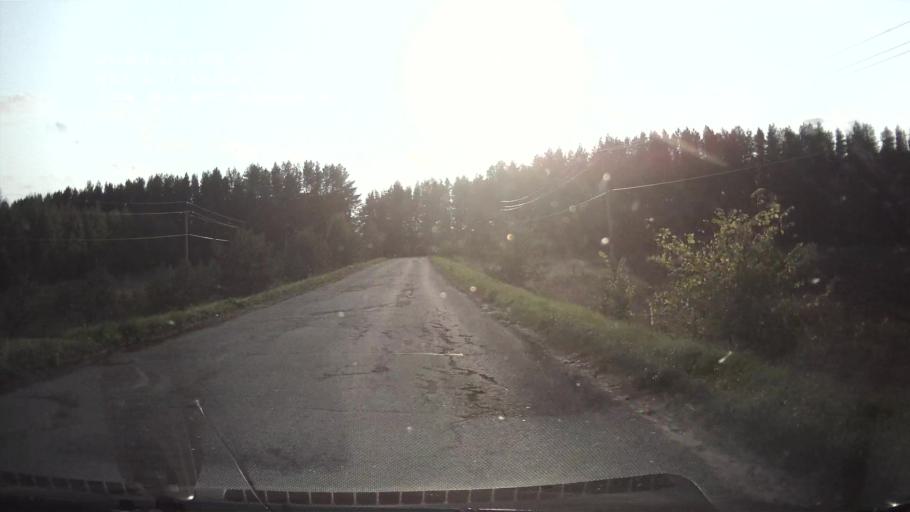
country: RU
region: Mariy-El
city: Kuzhener
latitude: 56.9514
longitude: 48.7526
